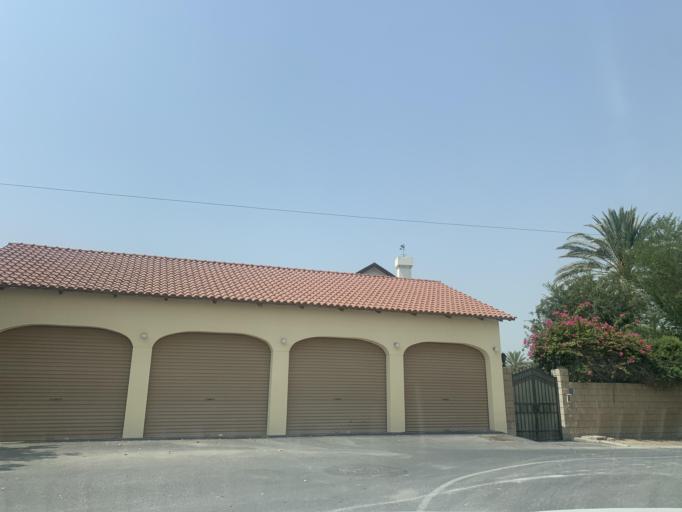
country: BH
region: Central Governorate
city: Madinat Hamad
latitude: 26.1637
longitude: 50.4500
